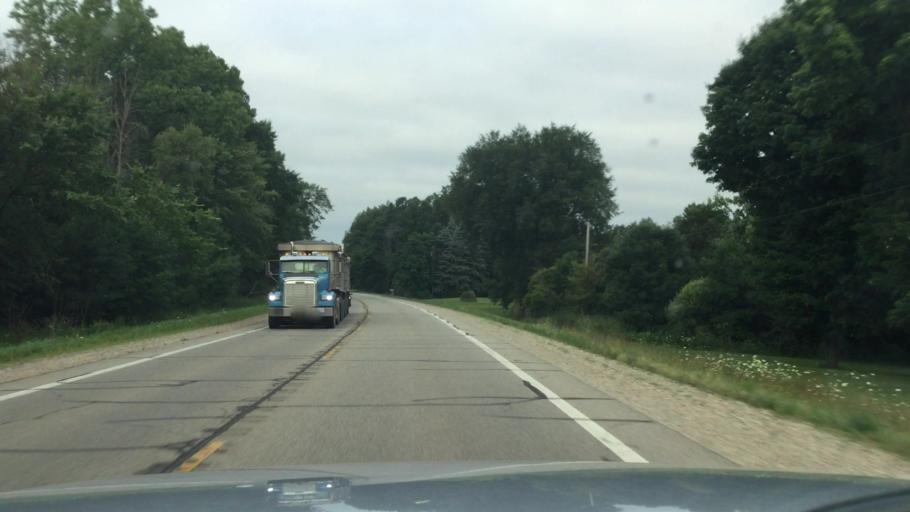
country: US
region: Michigan
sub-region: Montcalm County
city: Stanton
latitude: 43.1768
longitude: -85.1085
